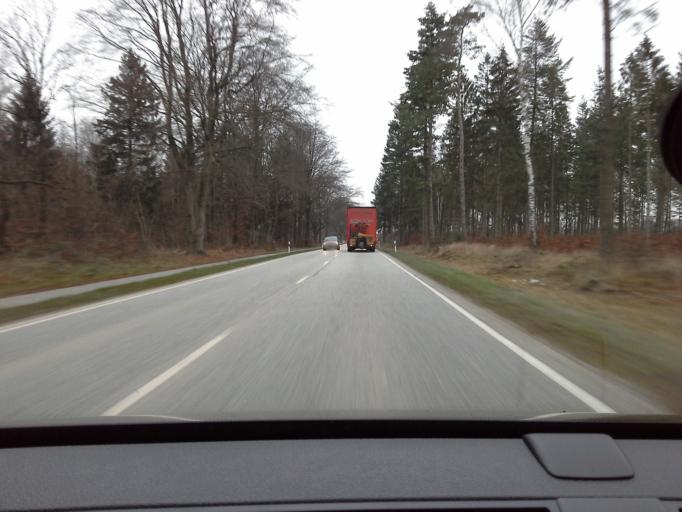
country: DE
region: Schleswig-Holstein
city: Lentfohrden
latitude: 53.8437
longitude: 9.8863
